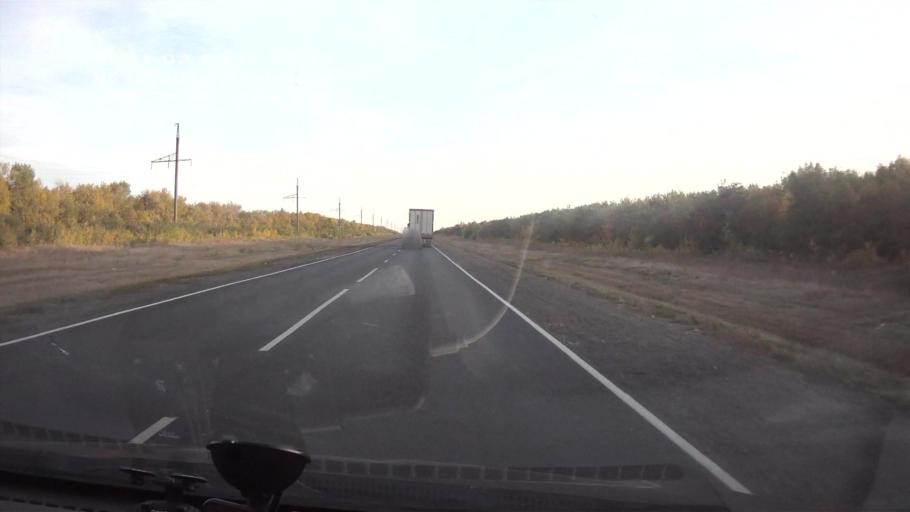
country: RU
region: Saratov
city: Krasnoarmeysk
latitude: 51.1385
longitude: 45.6501
